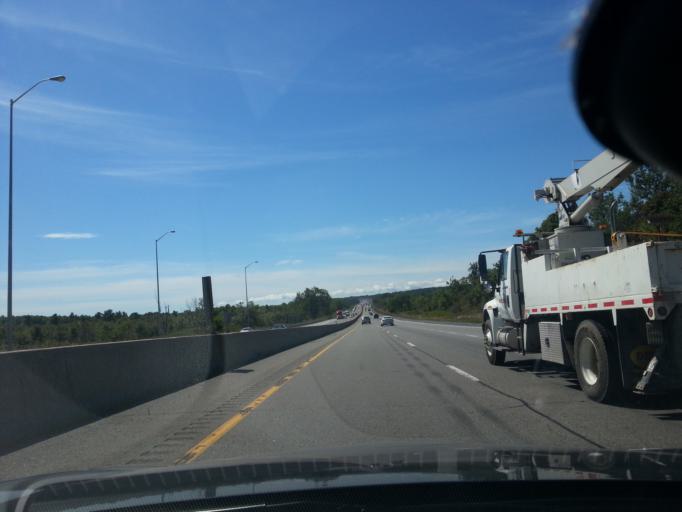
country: CA
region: Ontario
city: Kingston
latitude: 44.2867
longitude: -76.4362
